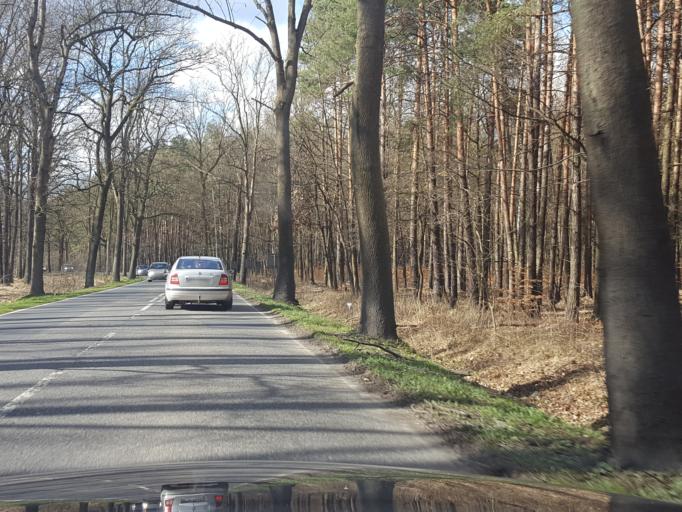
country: PL
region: Silesian Voivodeship
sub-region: Powiat pszczynski
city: Kobior
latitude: 50.0704
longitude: 18.9121
